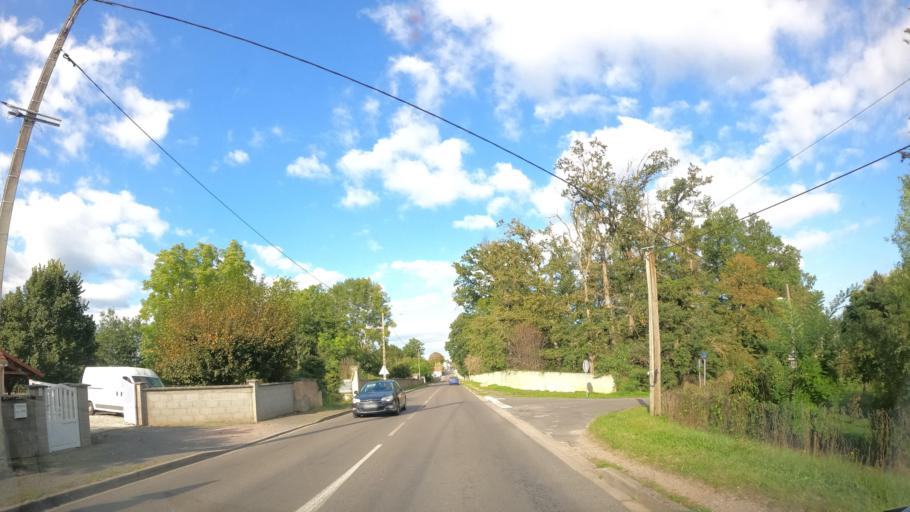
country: FR
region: Auvergne
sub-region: Departement de l'Allier
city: Dompierre-sur-Besbre
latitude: 46.5162
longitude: 3.6778
